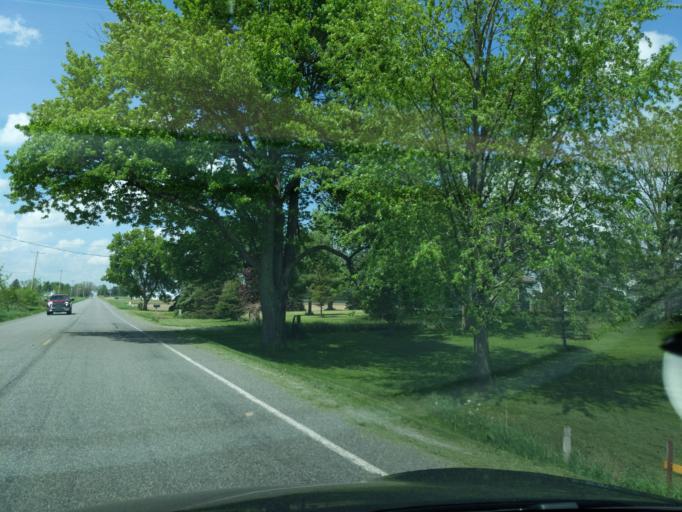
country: US
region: Michigan
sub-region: Ingham County
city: Mason
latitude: 42.6200
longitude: -84.4330
